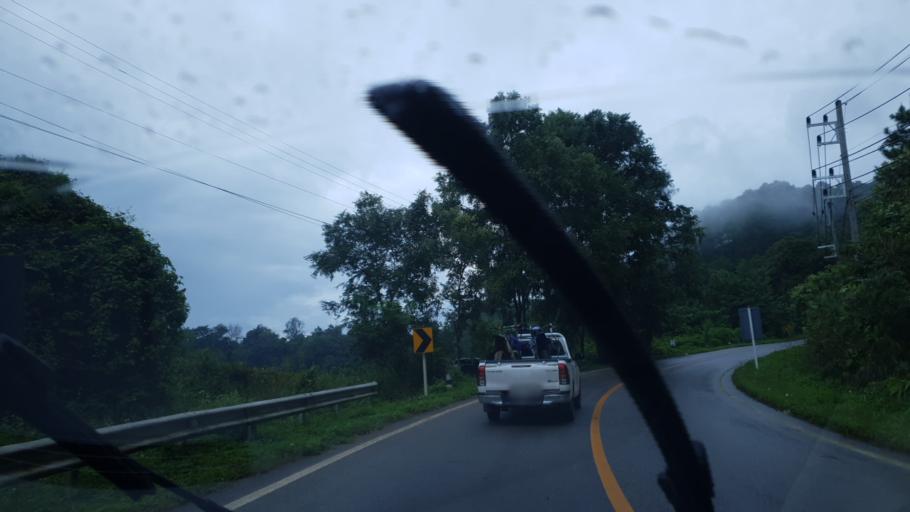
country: TH
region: Mae Hong Son
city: Ban Huai I Huak
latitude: 18.1631
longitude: 98.0540
